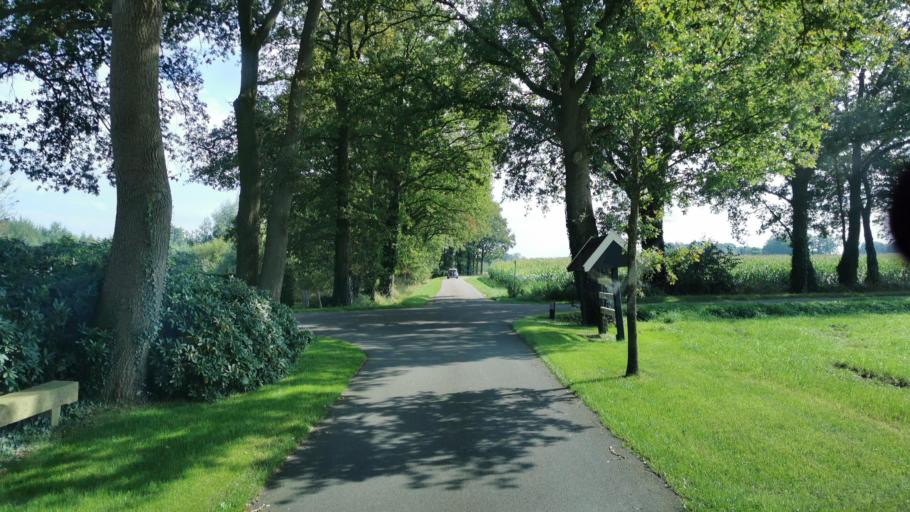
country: NL
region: Overijssel
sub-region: Gemeente Hengelo
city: Hengelo
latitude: 52.3217
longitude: 6.8136
